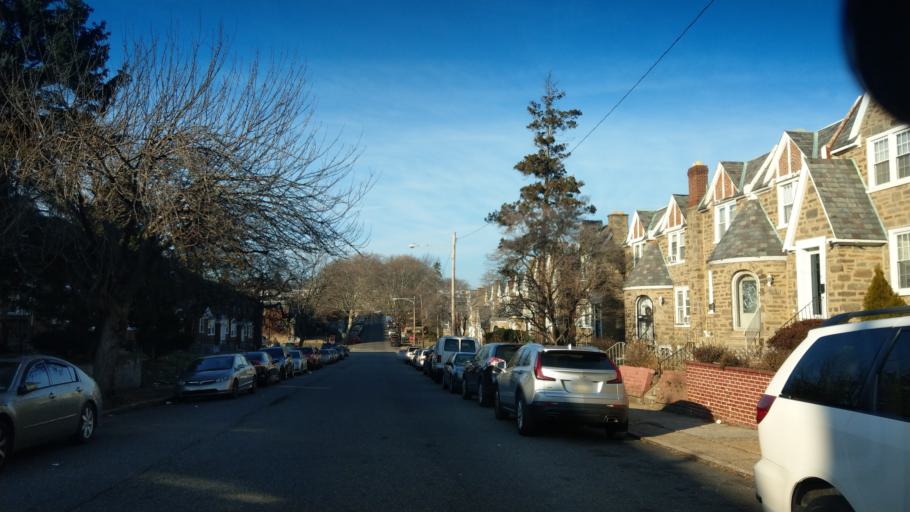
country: US
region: Pennsylvania
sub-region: Montgomery County
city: Rockledge
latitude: 40.0279
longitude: -75.1149
